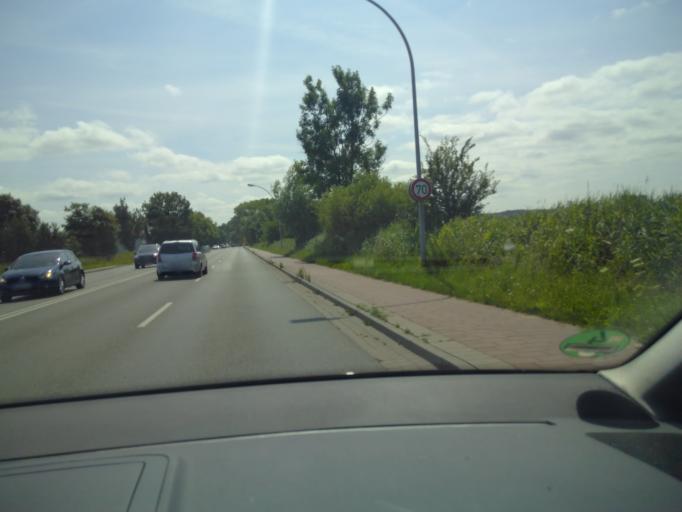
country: DE
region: Lower Saxony
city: Cuxhaven
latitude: 53.8402
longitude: 8.6833
